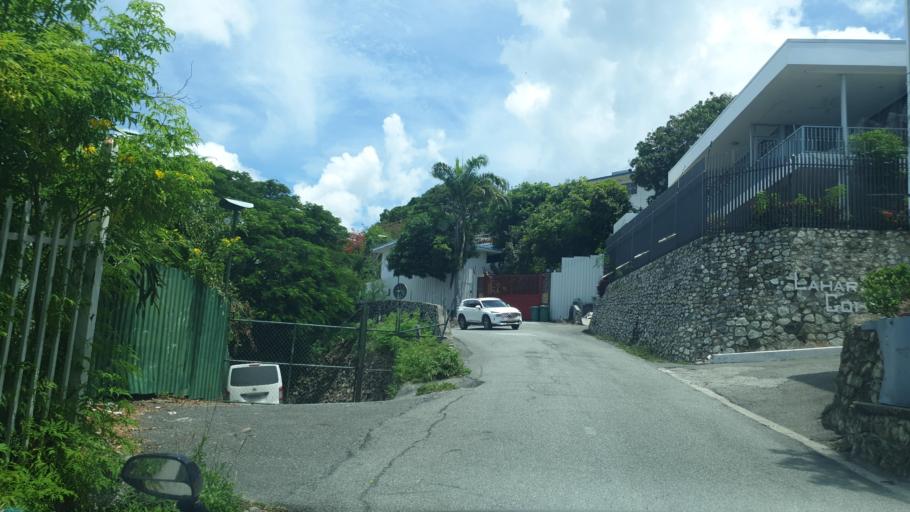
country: PG
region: National Capital
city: Port Moresby
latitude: -9.4772
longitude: 147.1536
